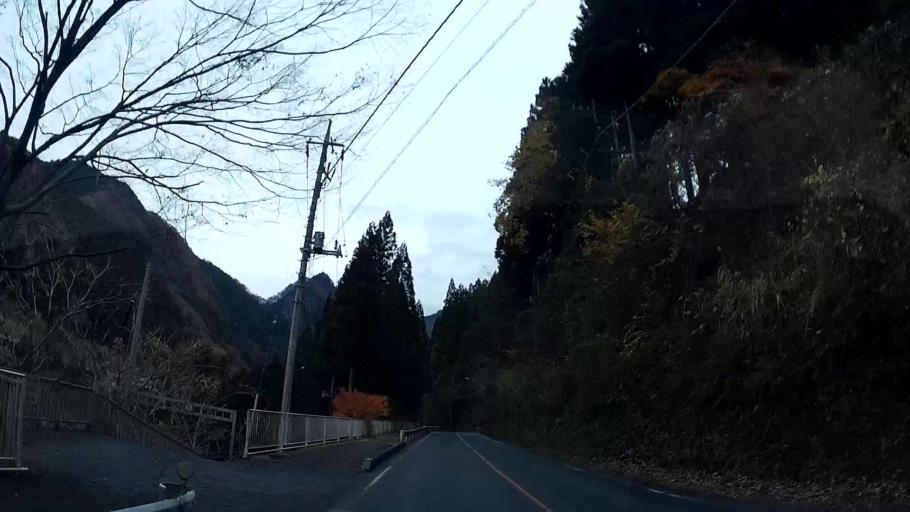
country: JP
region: Saitama
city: Chichibu
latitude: 35.9496
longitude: 138.9641
